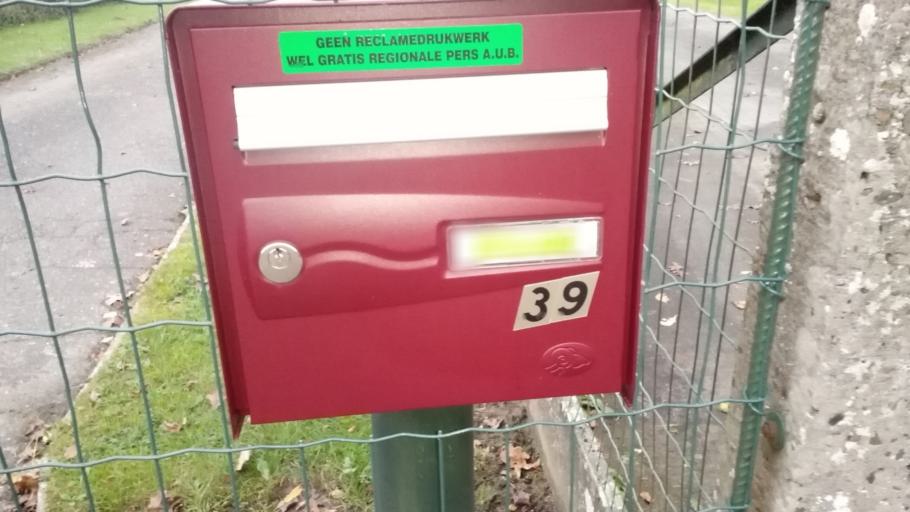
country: BE
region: Flanders
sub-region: Provincie Vlaams-Brabant
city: Aarschot
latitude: 51.0139
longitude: 4.8467
